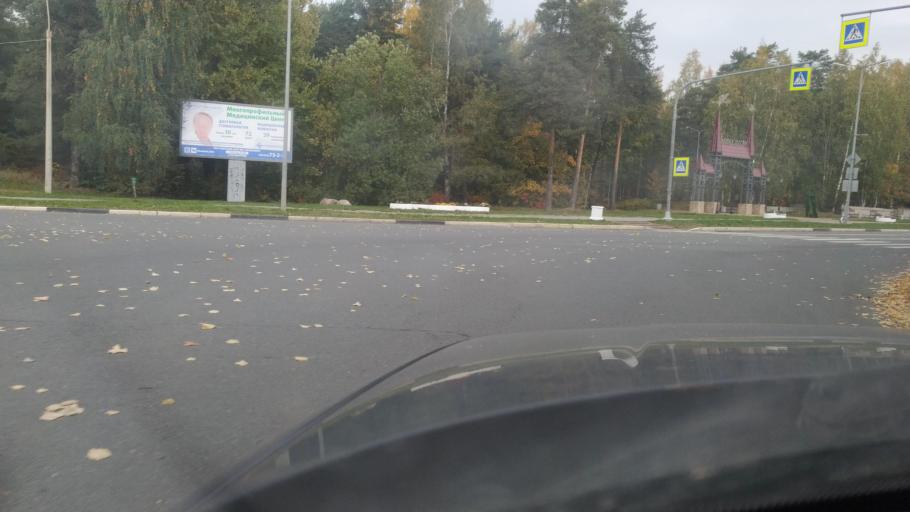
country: RU
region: Leningrad
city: Sosnovyy Bor
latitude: 59.8976
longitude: 29.0841
